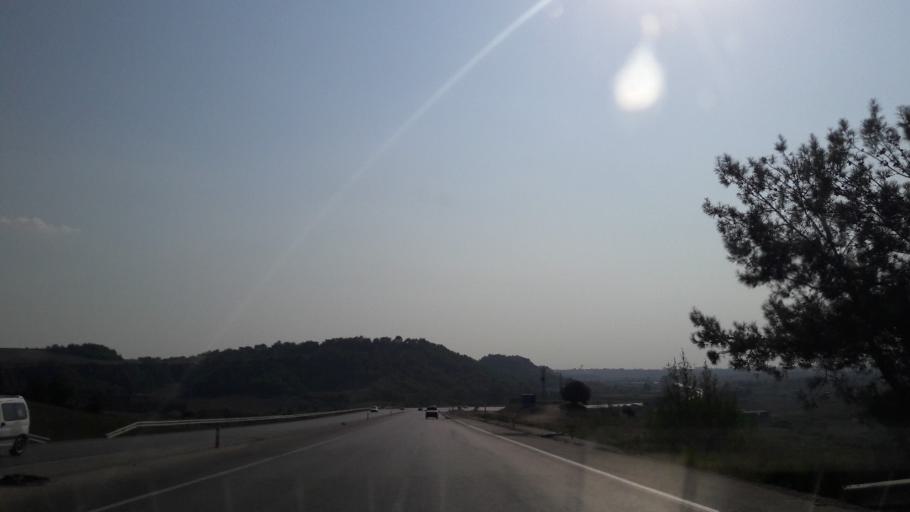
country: TR
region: Adana
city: Yuregir
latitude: 37.0787
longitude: 35.4729
